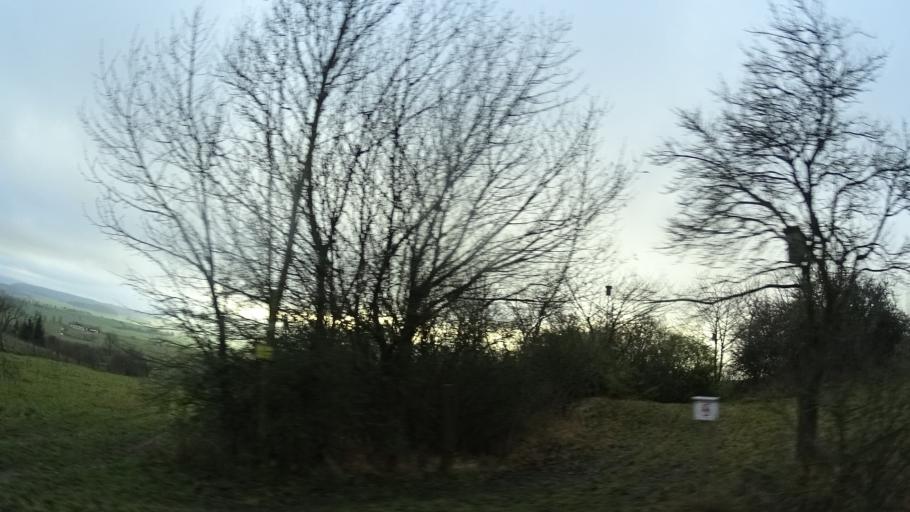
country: DE
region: Thuringia
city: Kuhndorf
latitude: 50.6135
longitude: 10.4840
